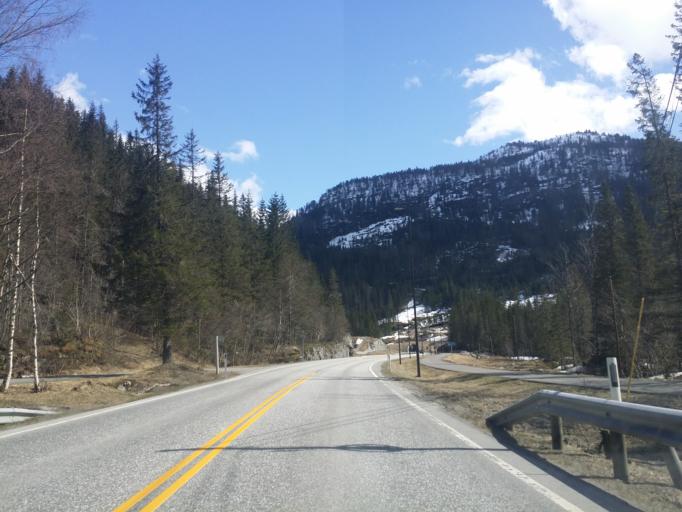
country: NO
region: Hordaland
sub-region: Granvin
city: Granvin
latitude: 60.5878
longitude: 6.6062
